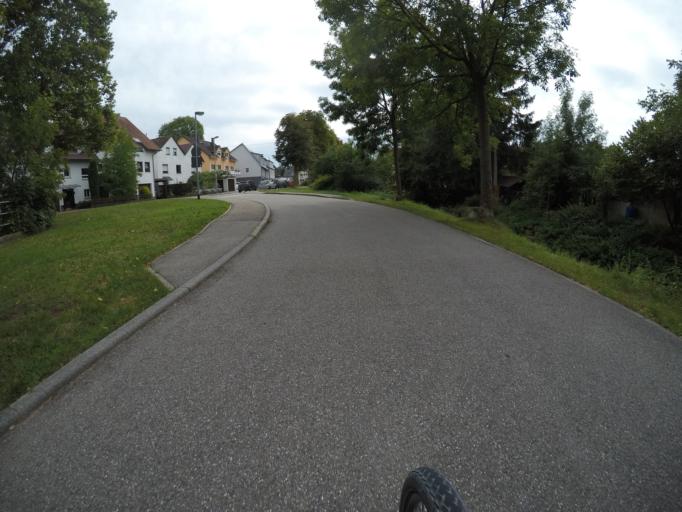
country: DE
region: Baden-Wuerttemberg
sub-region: Karlsruhe Region
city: Illingen
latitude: 48.9538
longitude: 8.9222
